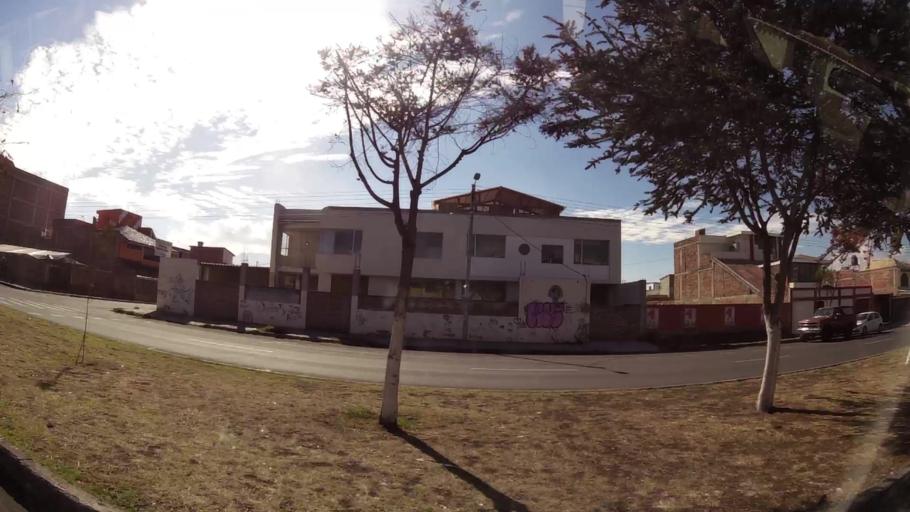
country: EC
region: Chimborazo
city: Riobamba
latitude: -1.6535
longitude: -78.6685
